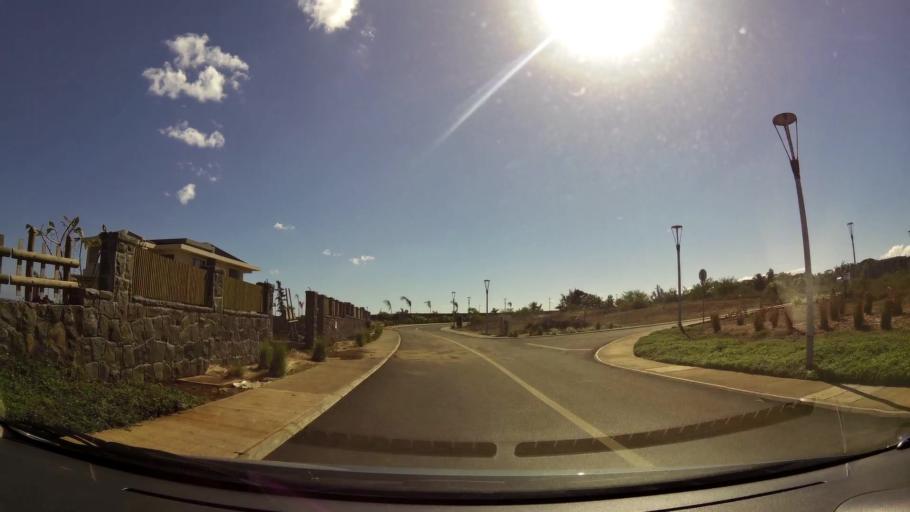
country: MU
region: Black River
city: Flic en Flac
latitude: -20.2690
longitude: 57.3826
